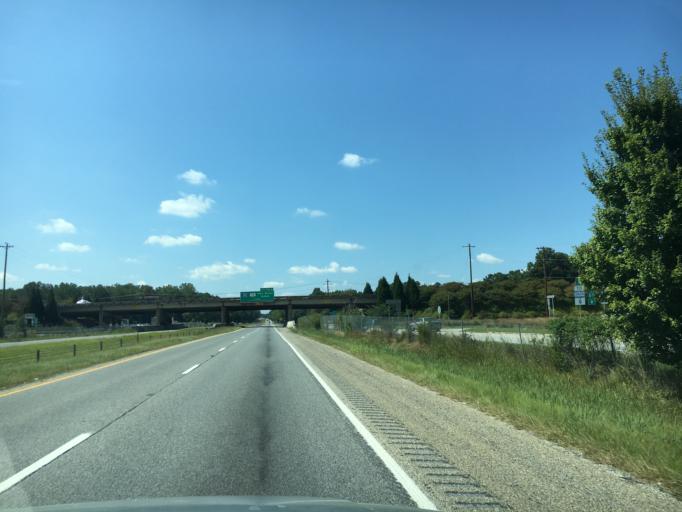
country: US
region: South Carolina
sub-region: Spartanburg County
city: Valley Falls
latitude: 34.9962
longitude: -81.9445
